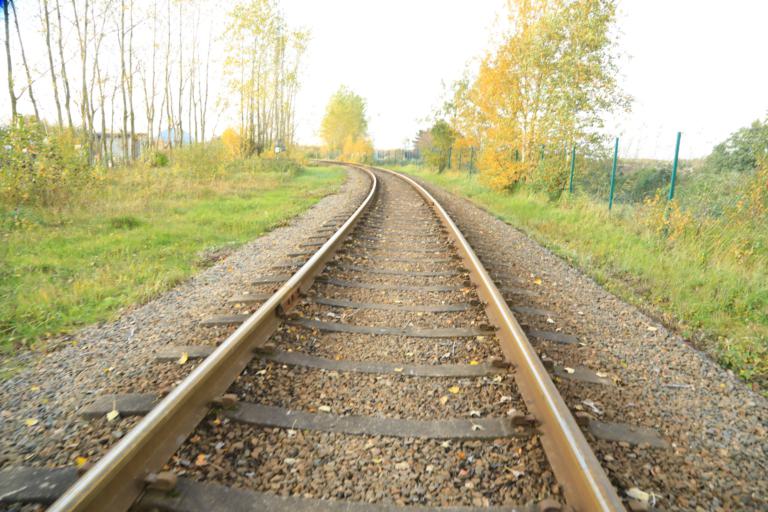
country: SE
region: Halland
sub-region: Varbergs Kommun
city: Varberg
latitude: 57.1208
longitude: 12.2462
